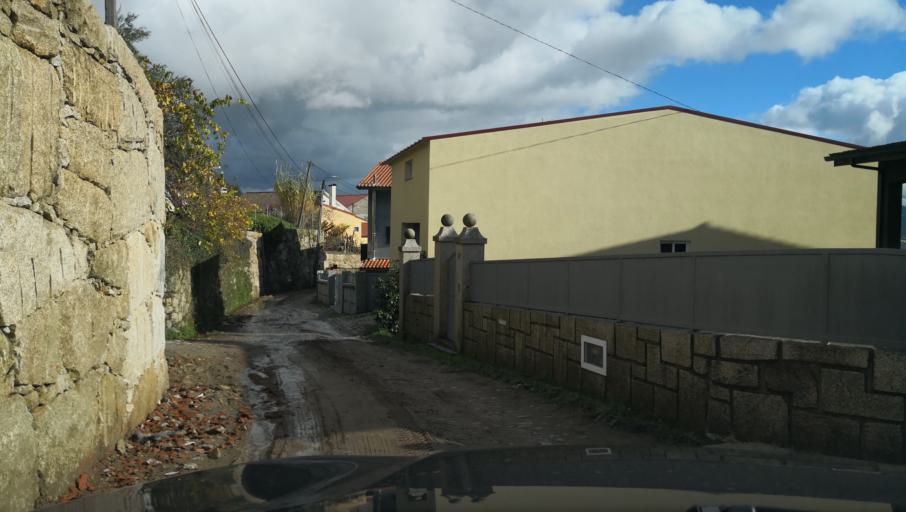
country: PT
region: Vila Real
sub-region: Vila Real
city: Vila Real
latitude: 41.3271
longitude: -7.7539
